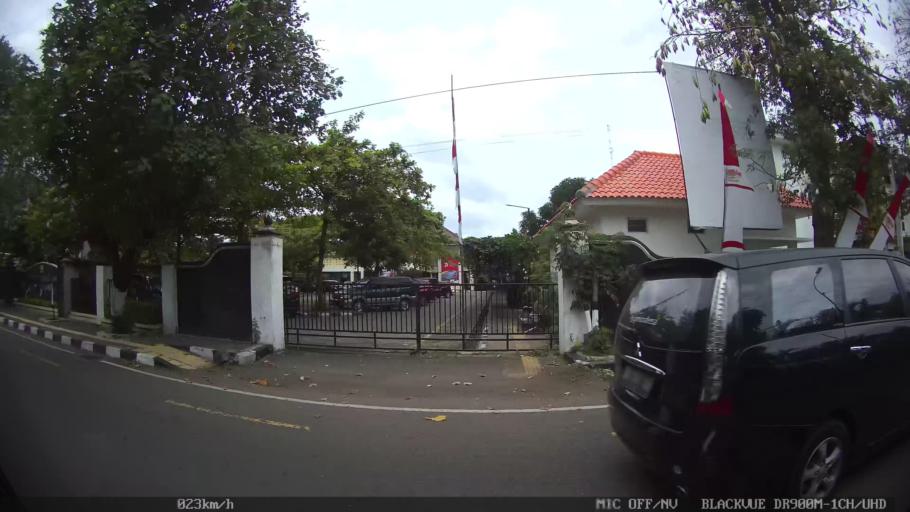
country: ID
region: Daerah Istimewa Yogyakarta
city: Yogyakarta
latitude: -7.7983
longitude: 110.3871
